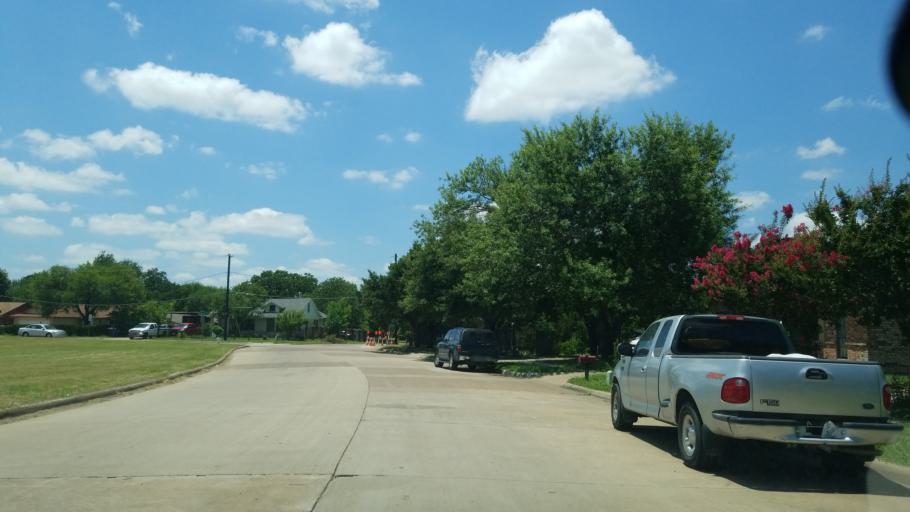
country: US
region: Texas
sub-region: Dallas County
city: Balch Springs
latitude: 32.7415
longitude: -96.7017
